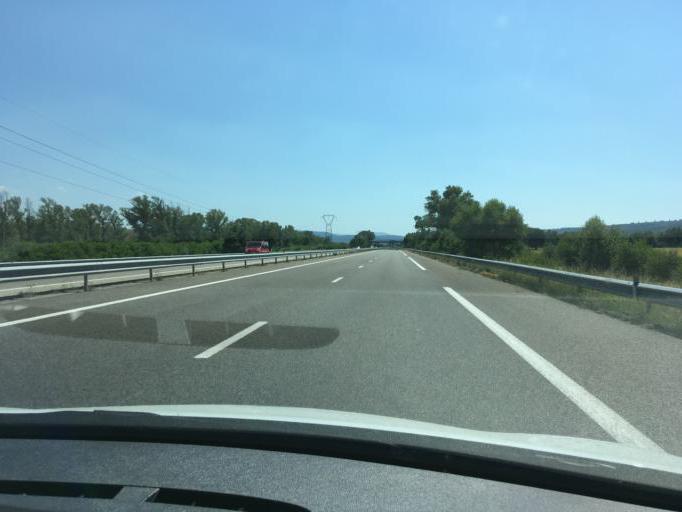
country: FR
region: Provence-Alpes-Cote d'Azur
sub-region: Departement des Alpes-de-Haute-Provence
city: Sainte-Tulle
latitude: 43.7489
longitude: 5.7652
